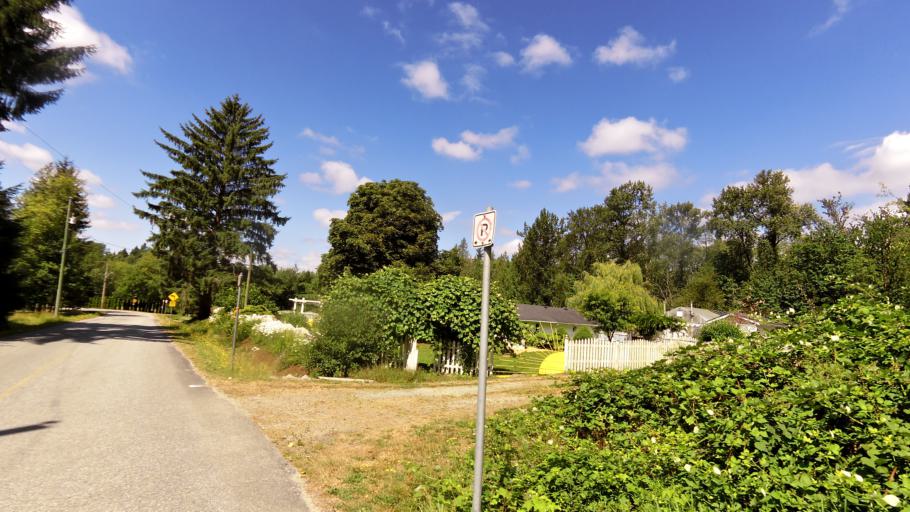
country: CA
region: British Columbia
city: Maple Ridge
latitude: 49.2157
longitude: -122.5249
